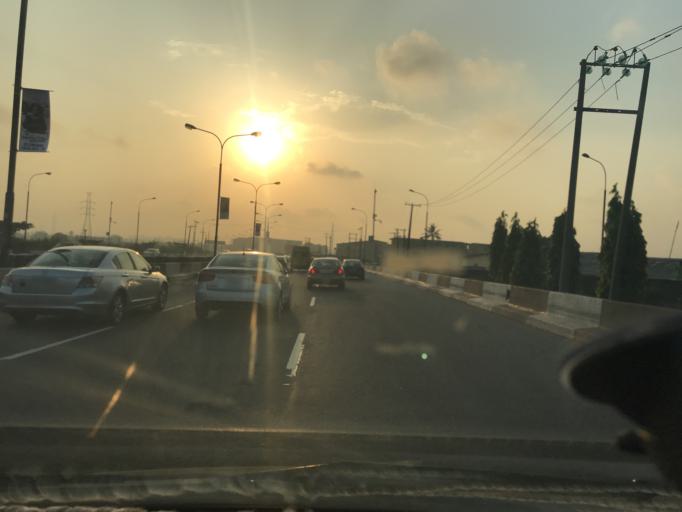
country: NG
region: Lagos
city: Lagos
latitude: 6.4601
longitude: 3.3977
